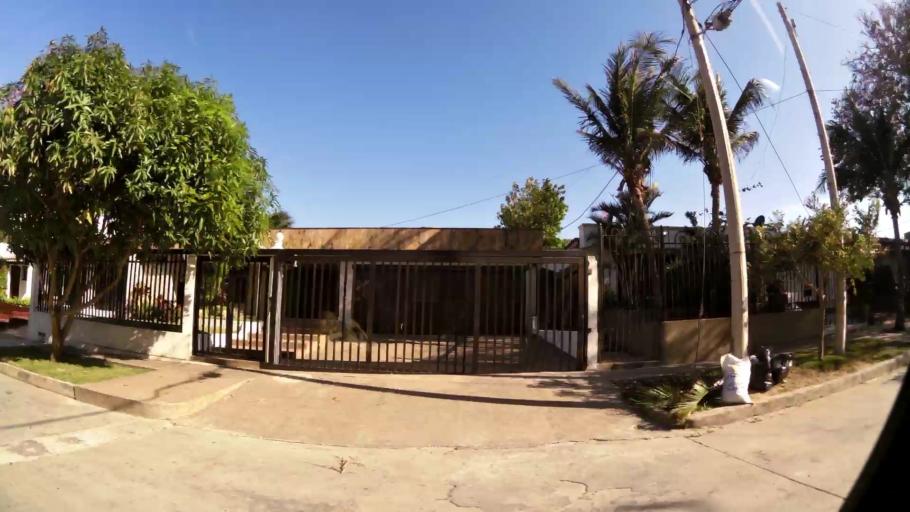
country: CO
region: Atlantico
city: Barranquilla
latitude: 10.9973
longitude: -74.8279
